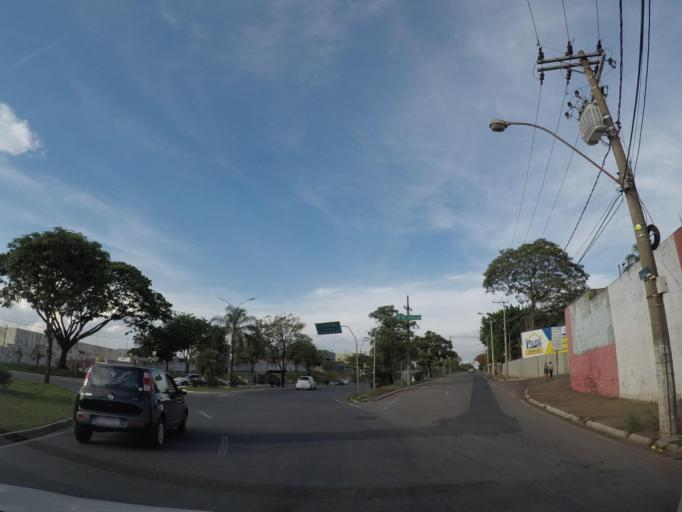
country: BR
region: Sao Paulo
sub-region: Sumare
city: Sumare
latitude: -22.8194
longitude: -47.2622
